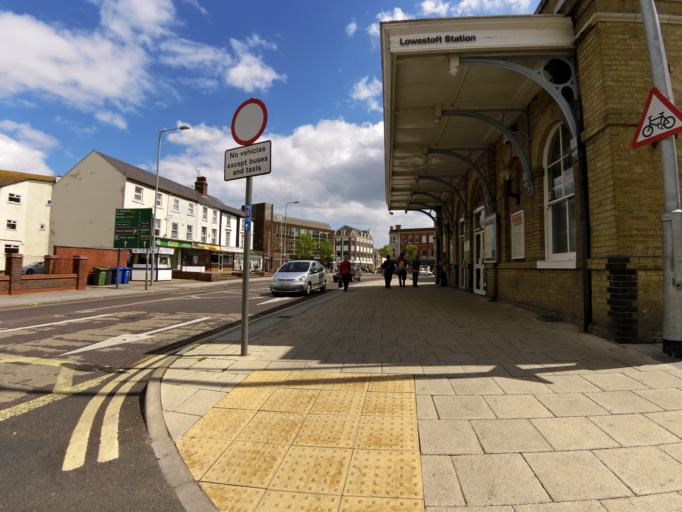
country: GB
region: England
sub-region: Suffolk
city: Lowestoft
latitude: 52.4745
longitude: 1.7495
